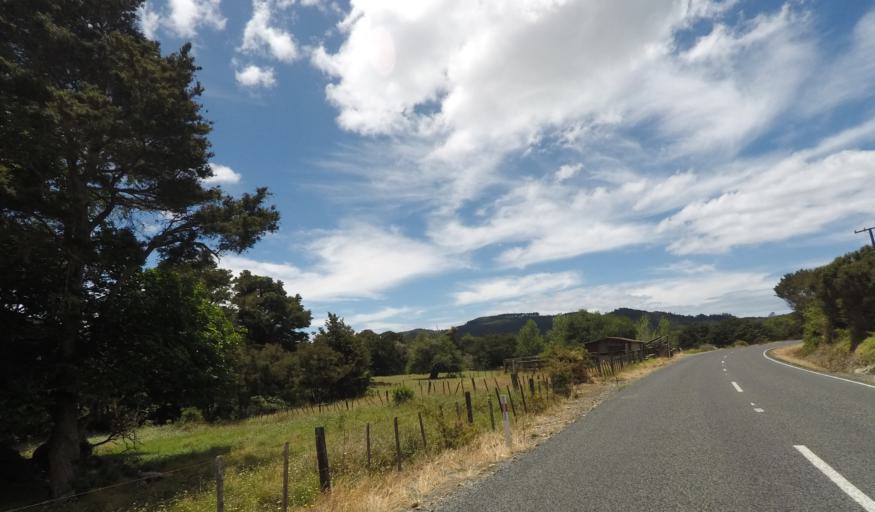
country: NZ
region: Northland
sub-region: Whangarei
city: Ngunguru
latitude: -35.5072
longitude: 174.4212
